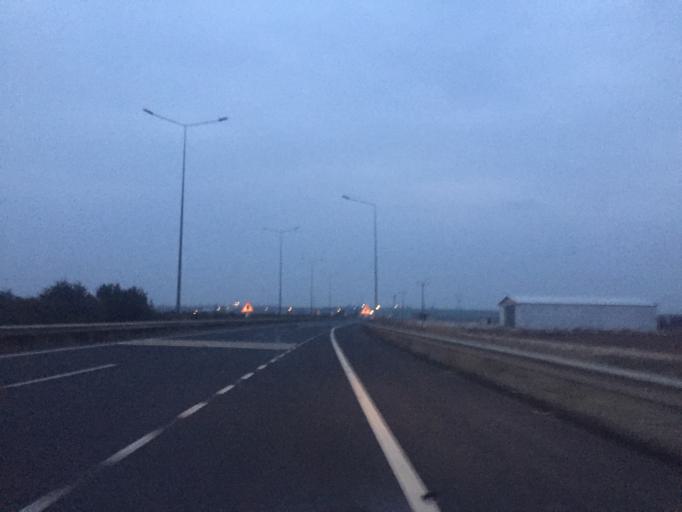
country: TR
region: Sanliurfa
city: Camlidere
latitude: 37.1606
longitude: 39.0234
